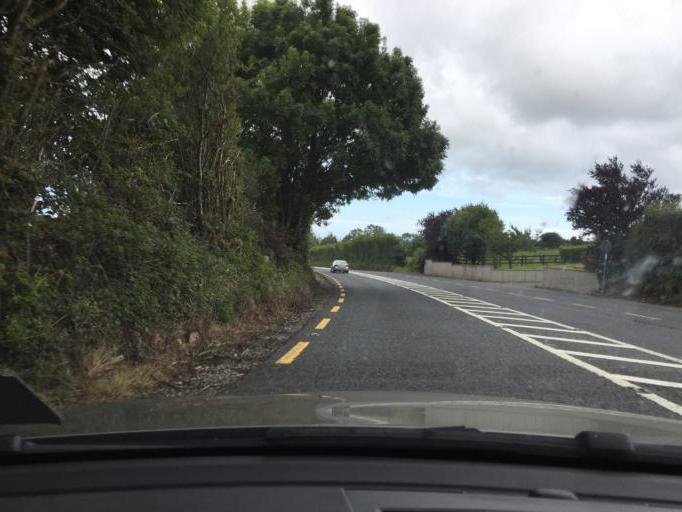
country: IE
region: Munster
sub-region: Waterford
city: Dungarvan
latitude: 52.1188
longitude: -7.5613
